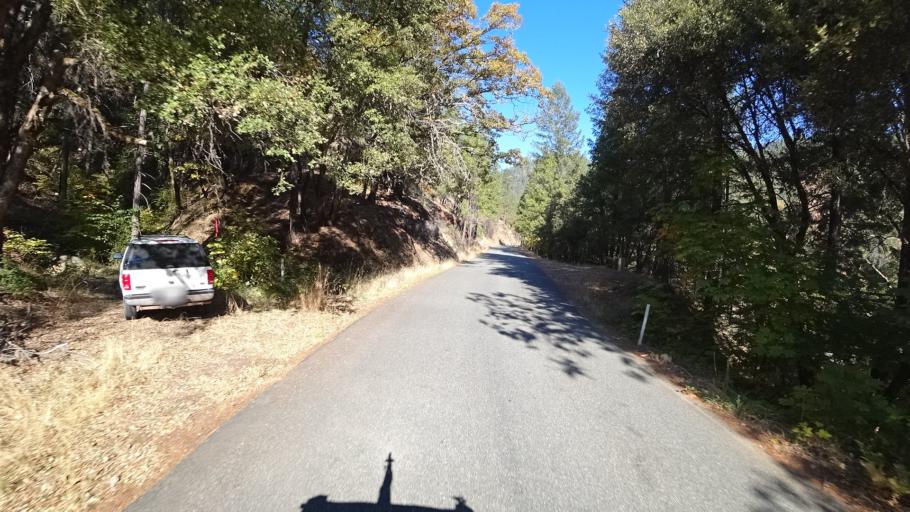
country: US
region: California
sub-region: Siskiyou County
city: Happy Camp
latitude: 41.7571
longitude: -123.0142
